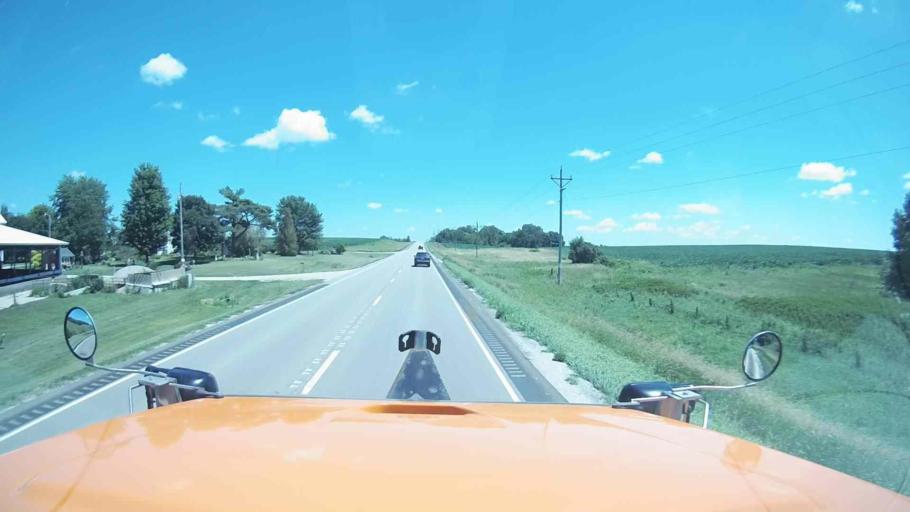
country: US
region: Iowa
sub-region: Benton County
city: Urbana
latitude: 42.2247
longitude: -91.9530
